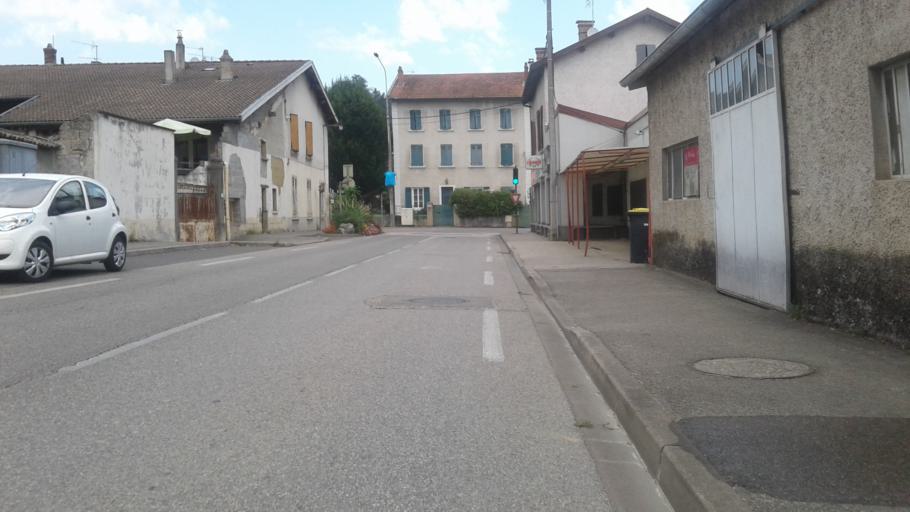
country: FR
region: Rhone-Alpes
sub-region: Departement de l'Ain
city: Beynost
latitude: 45.8361
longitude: 5.0050
